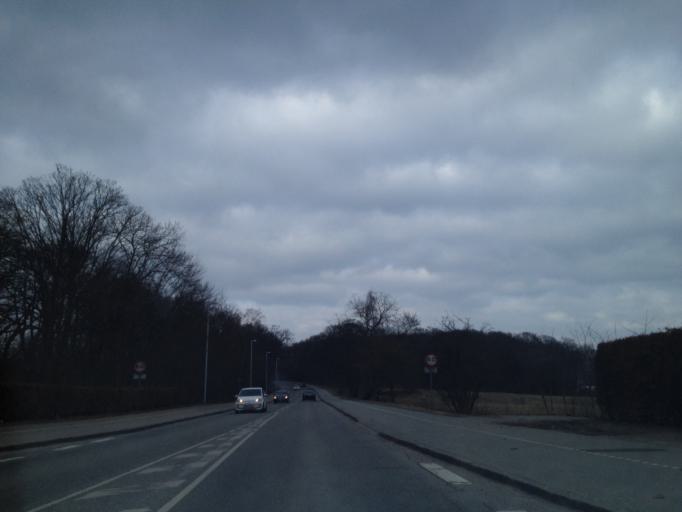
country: DK
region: Capital Region
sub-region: Fredensborg Kommune
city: Humlebaek
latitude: 55.9726
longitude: 12.5422
